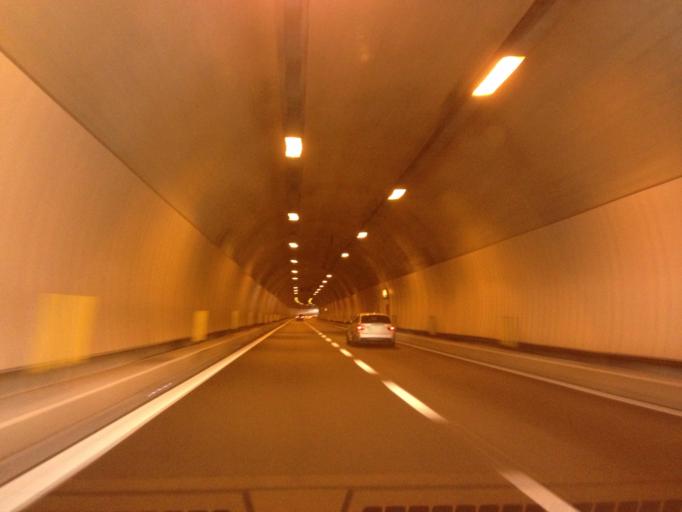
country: IT
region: Trentino-Alto Adige
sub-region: Bolzano
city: Velturno
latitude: 46.6493
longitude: 11.5888
